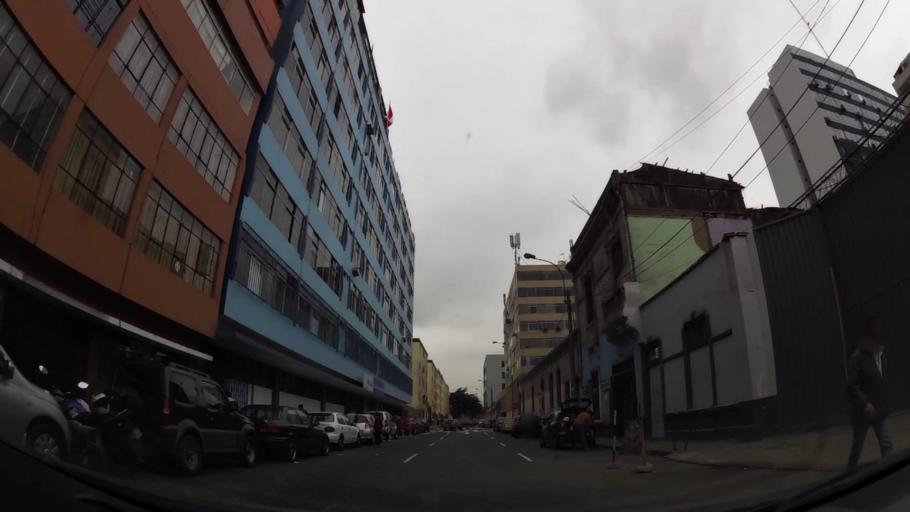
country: PE
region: Lima
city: Lima
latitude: -12.0628
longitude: -77.0395
